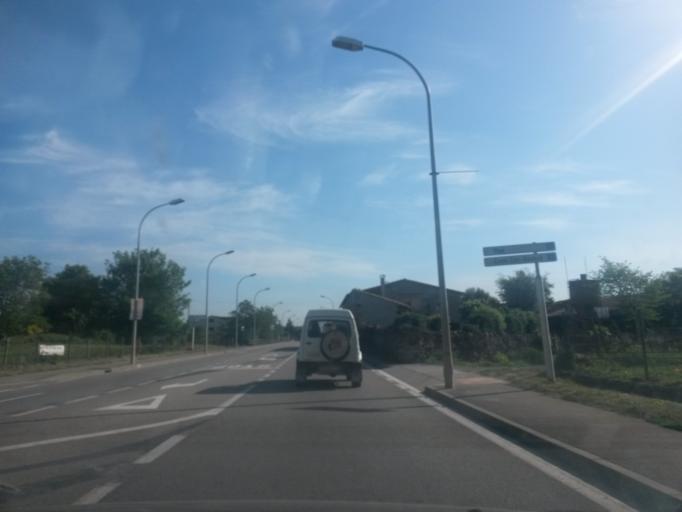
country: ES
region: Catalonia
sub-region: Provincia de Girona
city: Olot
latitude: 42.1610
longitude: 2.4691
